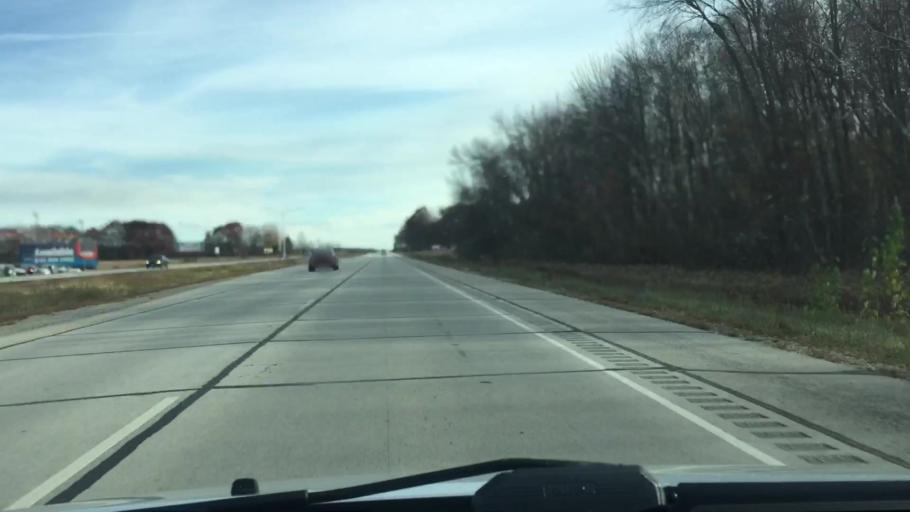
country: US
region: Wisconsin
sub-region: Brown County
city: Oneida
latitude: 44.5727
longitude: -88.1617
